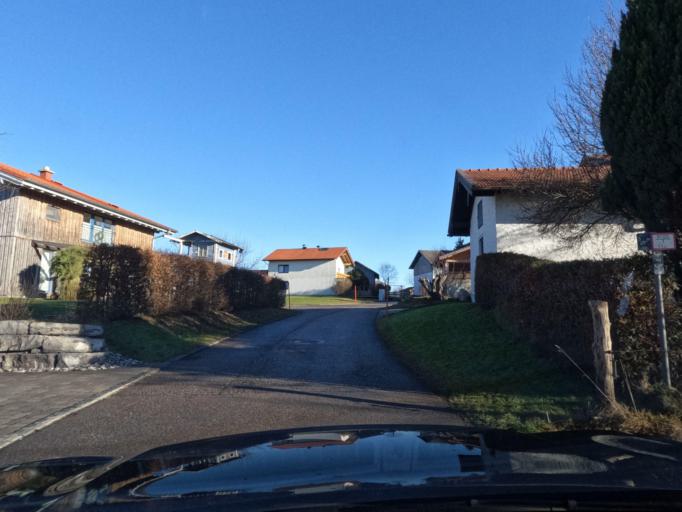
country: DE
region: Bavaria
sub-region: Upper Bavaria
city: Sankt Leonhard am Wonneberg
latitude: 47.8955
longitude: 12.7024
